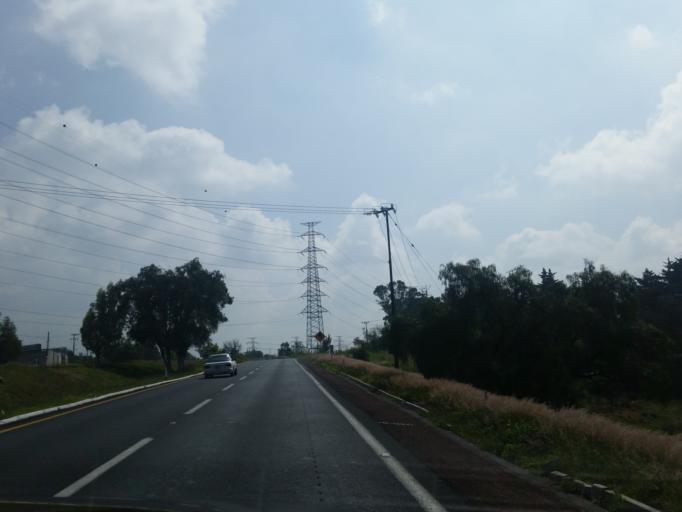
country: MX
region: Morelos
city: Xometla
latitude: 19.6584
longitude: -98.8750
